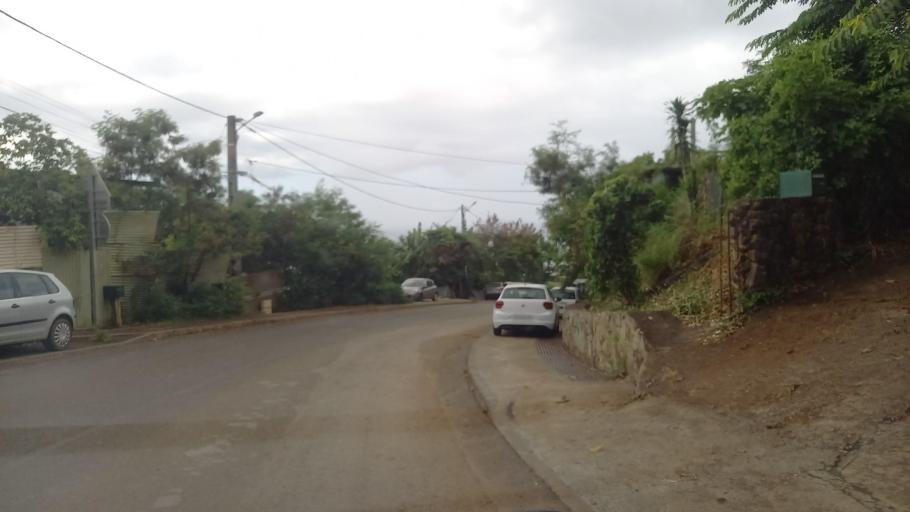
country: YT
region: Sada
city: Sada
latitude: -12.8485
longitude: 45.1043
